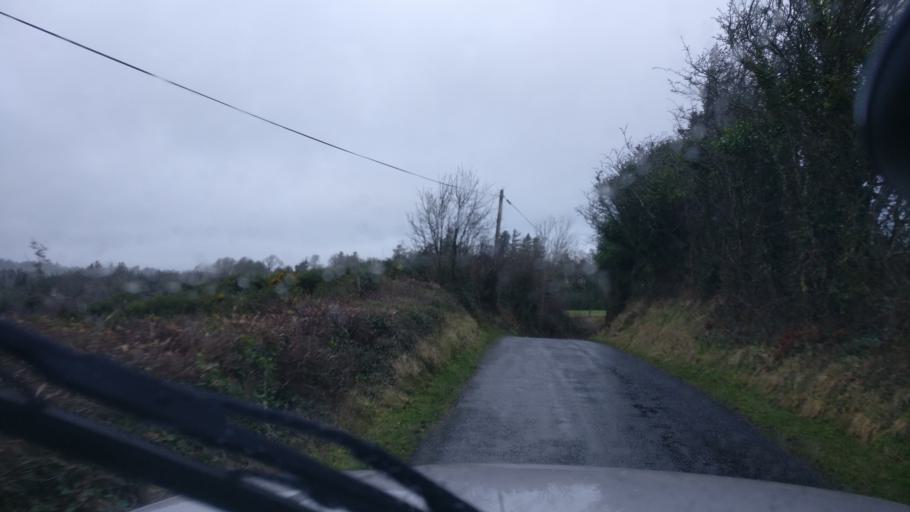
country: IE
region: Connaught
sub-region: County Galway
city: Loughrea
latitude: 53.1566
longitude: -8.6101
